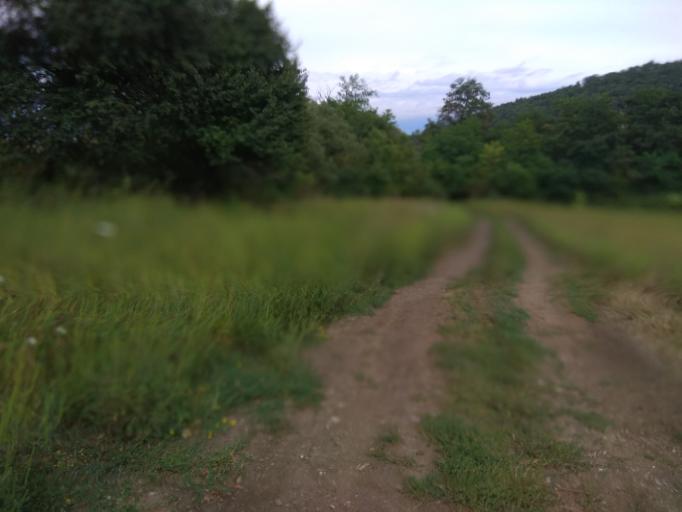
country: HU
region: Heves
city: Belapatfalva
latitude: 48.0184
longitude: 20.2938
